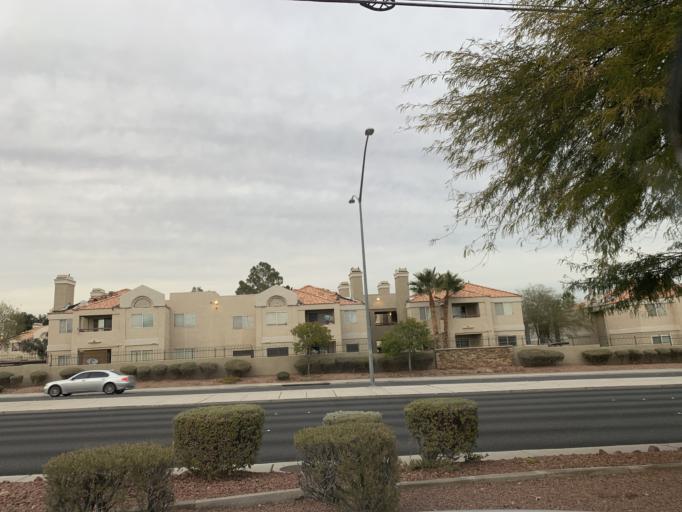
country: US
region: Nevada
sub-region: Clark County
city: Spring Valley
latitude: 36.1588
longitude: -115.2824
